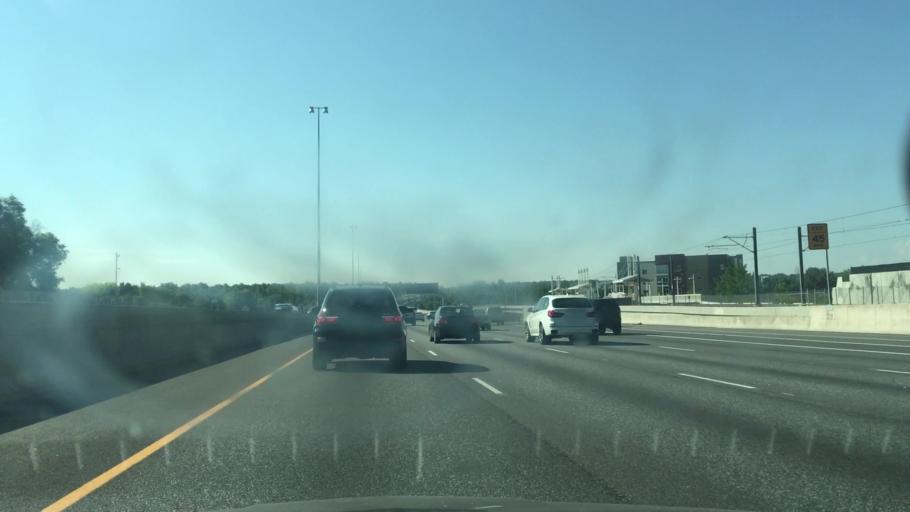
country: US
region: Colorado
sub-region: Arapahoe County
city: Glendale
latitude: 39.6691
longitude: -104.9280
